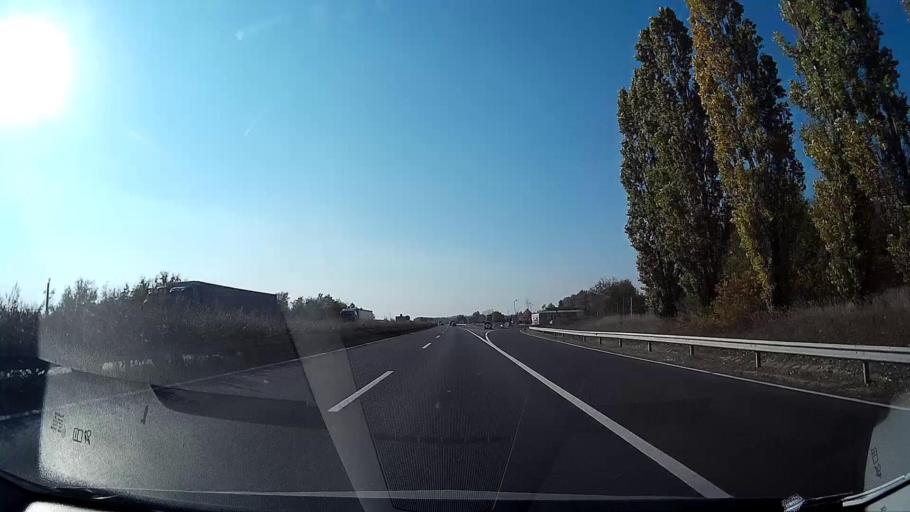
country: HU
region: Pest
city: Zsambek
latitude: 47.5110
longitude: 18.7397
